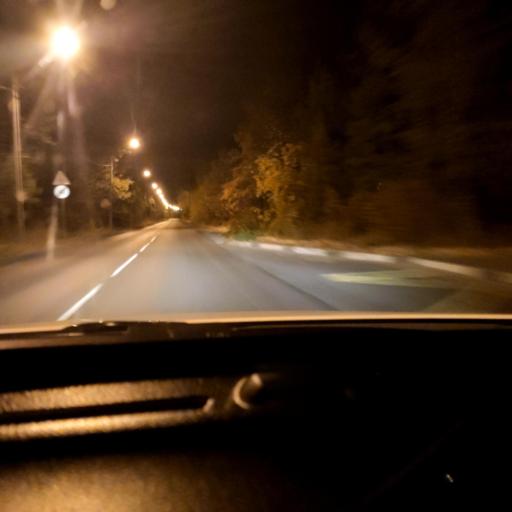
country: RU
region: Voronezj
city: Somovo
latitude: 51.7198
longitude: 39.3216
